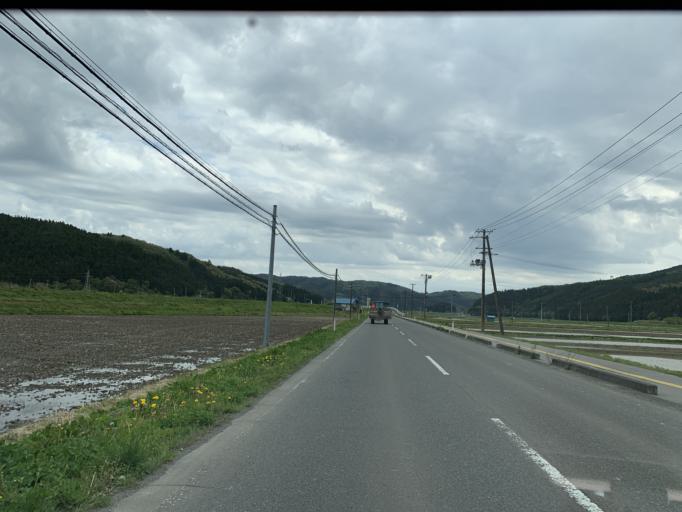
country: JP
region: Iwate
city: Ichinoseki
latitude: 38.7642
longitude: 141.3271
